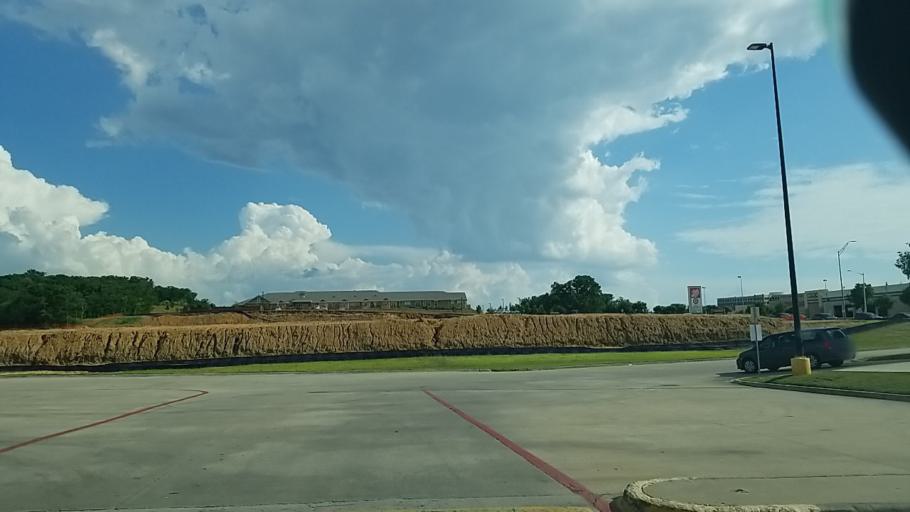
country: US
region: Texas
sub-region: Denton County
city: Denton
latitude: 33.1909
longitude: -97.0949
